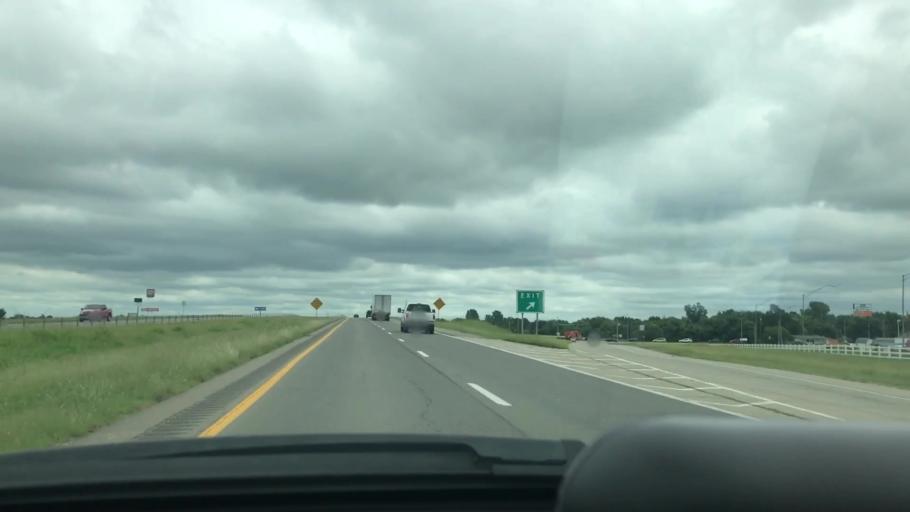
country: US
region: Oklahoma
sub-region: McIntosh County
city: Checotah
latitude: 35.4721
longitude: -95.5375
